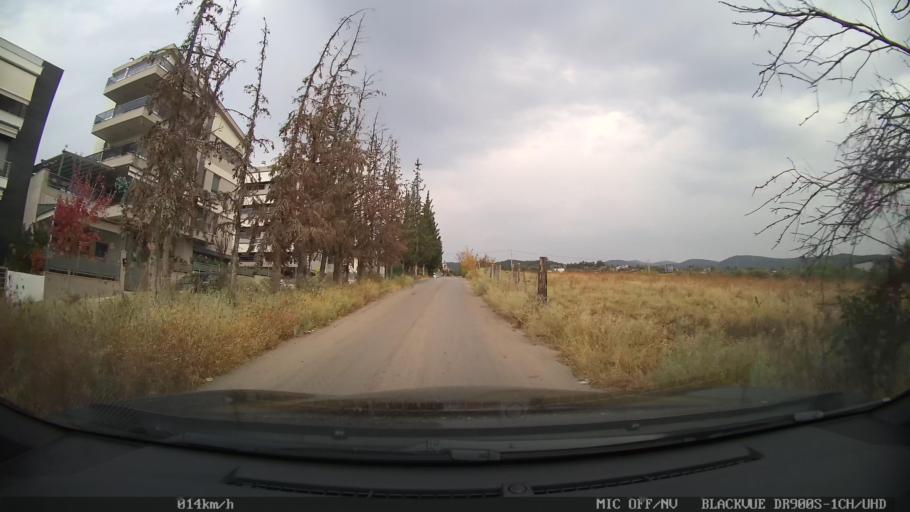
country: GR
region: Central Macedonia
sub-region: Nomos Thessalonikis
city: Pylaia
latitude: 40.6093
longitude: 22.9968
